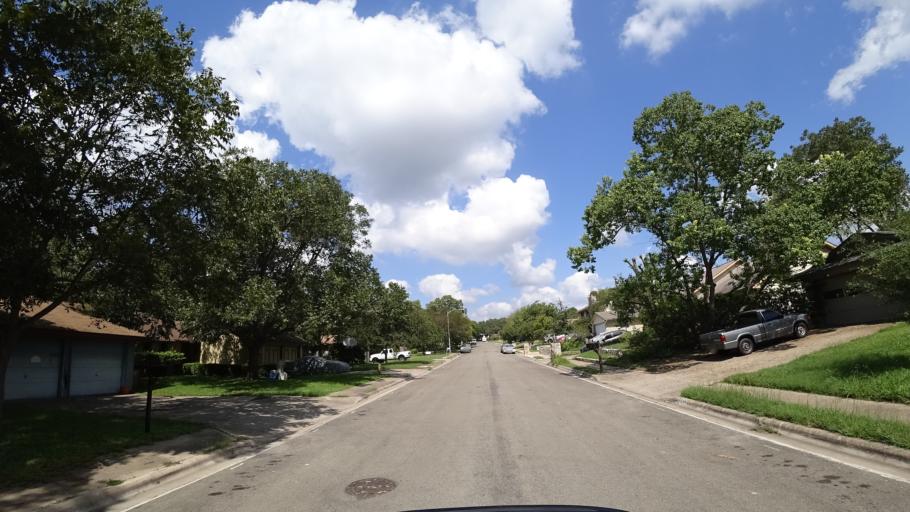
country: US
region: Texas
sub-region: Travis County
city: Onion Creek
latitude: 30.1881
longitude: -97.7877
